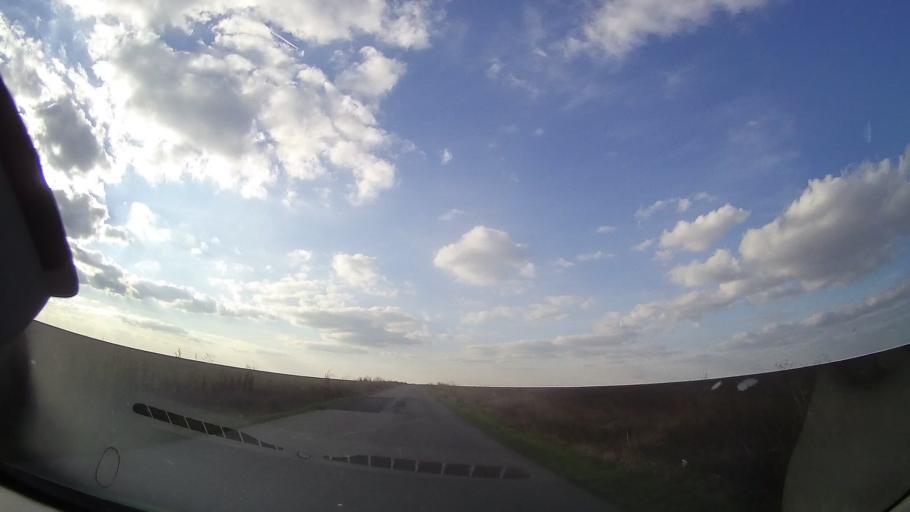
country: RO
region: Constanta
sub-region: Comuna Negru Voda
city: Negru Voda
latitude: 43.8223
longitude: 28.1566
